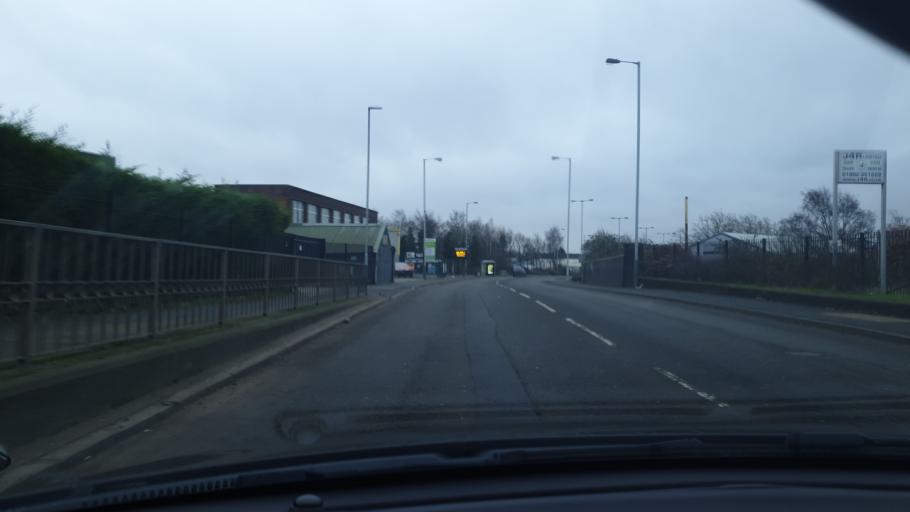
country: GB
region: England
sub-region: Wolverhampton
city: Wolverhampton
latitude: 52.5847
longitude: -2.1118
